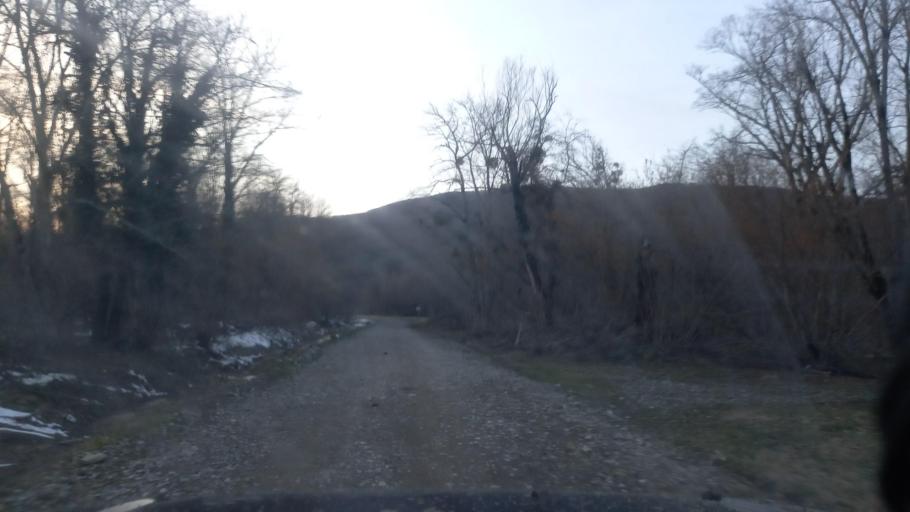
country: RU
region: Krasnodarskiy
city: Smolenskaya
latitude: 44.6228
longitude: 38.8238
